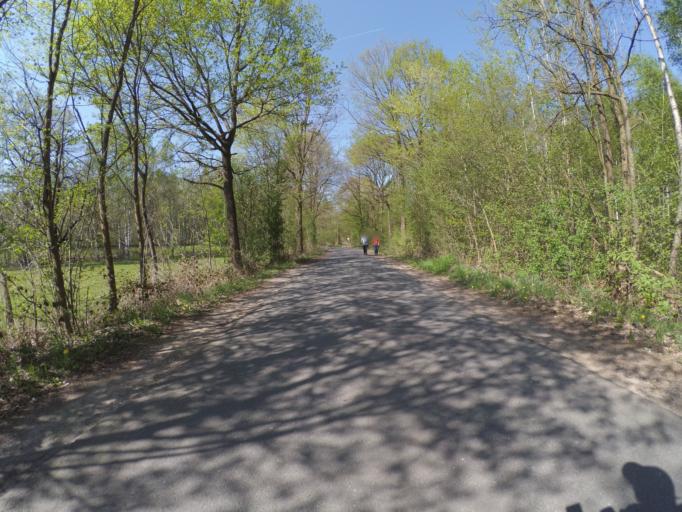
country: DE
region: North Rhine-Westphalia
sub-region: Regierungsbezirk Munster
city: Ascheberg
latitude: 51.8412
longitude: 7.5940
